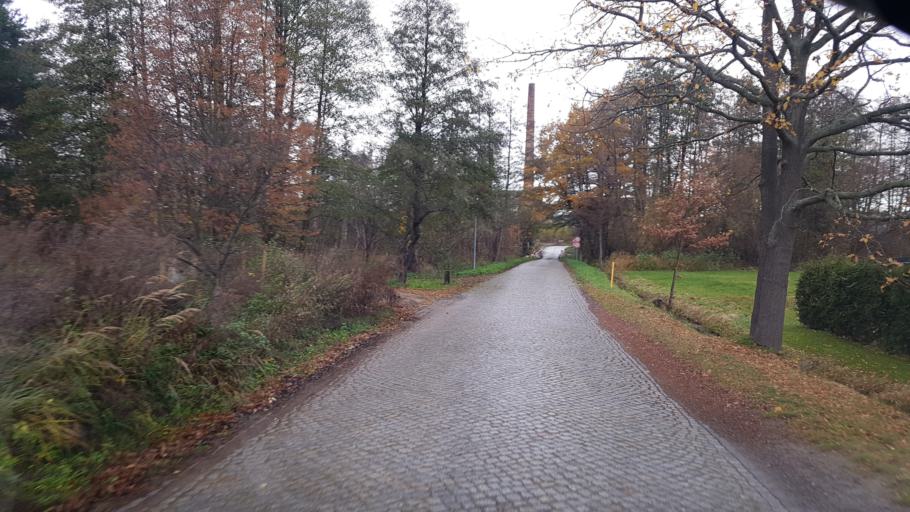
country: DE
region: Brandenburg
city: Ortrand
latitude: 51.3715
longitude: 13.7682
